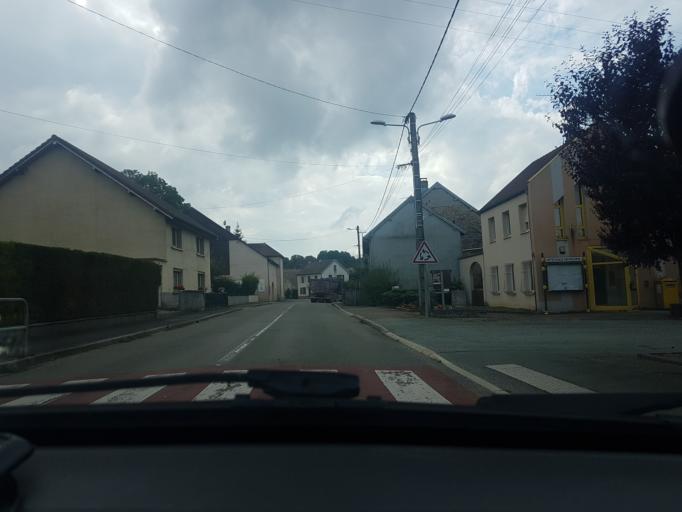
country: FR
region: Franche-Comte
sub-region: Departement du Doubs
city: Arcey
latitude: 47.5859
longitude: 6.6828
